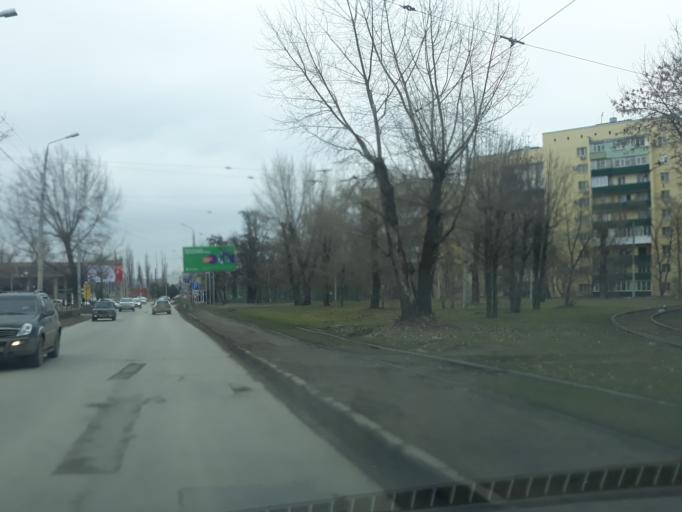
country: RU
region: Rostov
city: Taganrog
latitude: 47.2446
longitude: 38.8912
